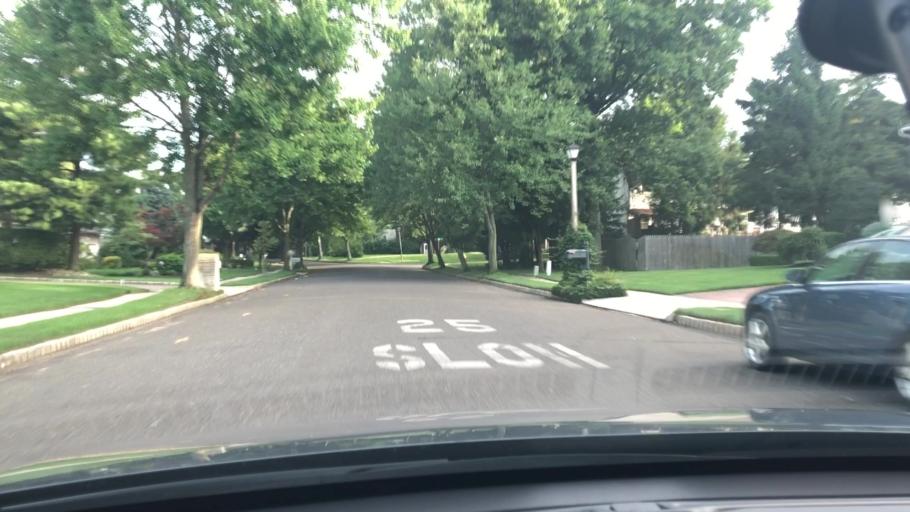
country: US
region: New Jersey
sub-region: Middlesex County
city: East Brunswick
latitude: 40.4206
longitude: -74.4271
